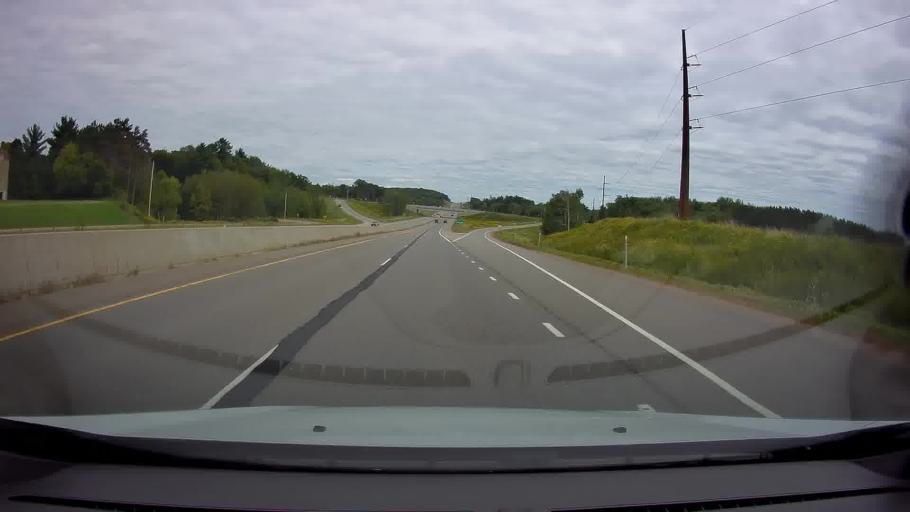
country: US
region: Wisconsin
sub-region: Marathon County
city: Marathon
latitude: 44.9439
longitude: -89.7912
